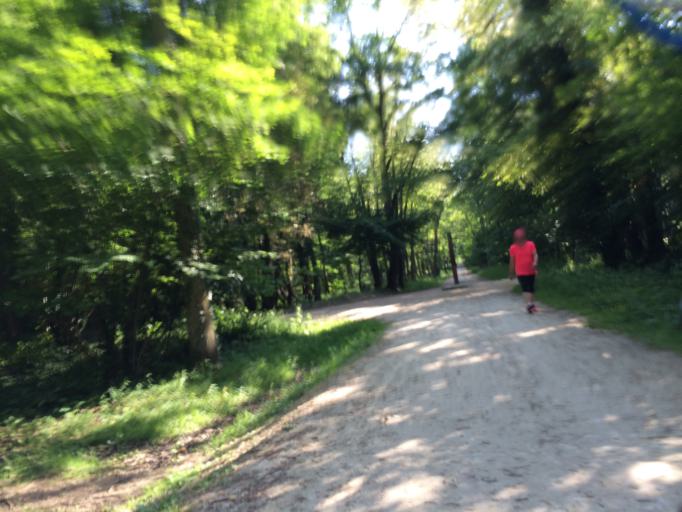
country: FR
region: Ile-de-France
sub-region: Departement de l'Essonne
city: Fleury-Merogis
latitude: 48.6342
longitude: 2.3520
